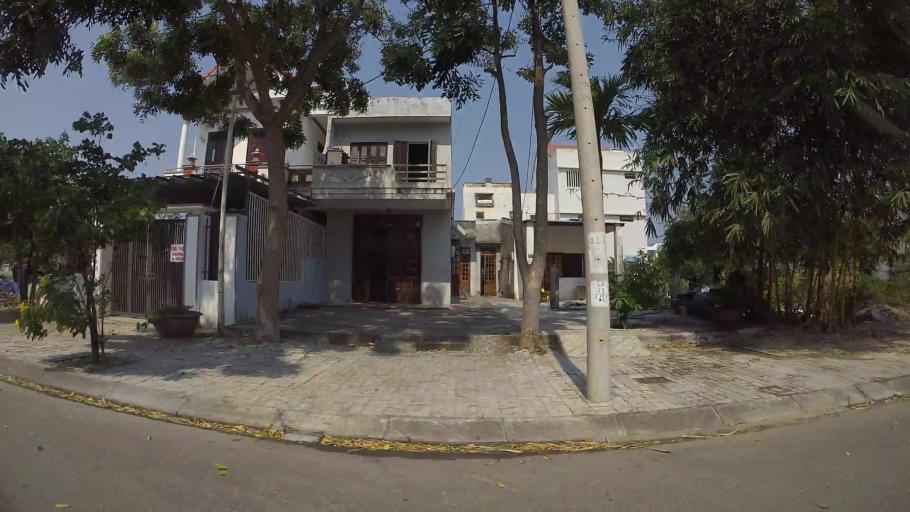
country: VN
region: Da Nang
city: Ngu Hanh Son
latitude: 15.9825
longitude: 108.2730
